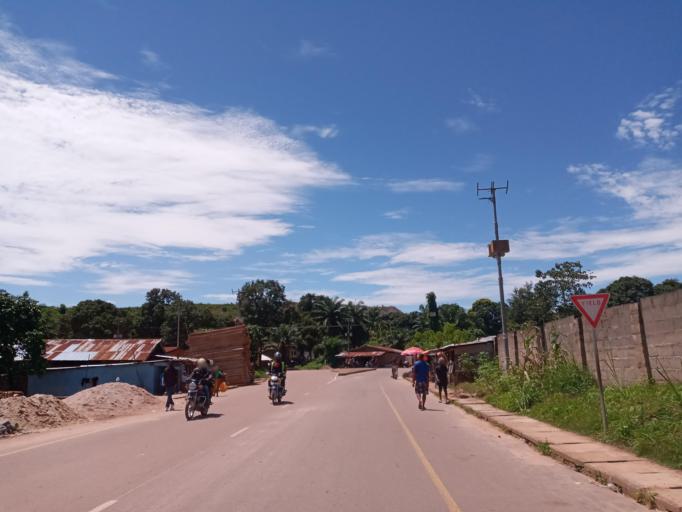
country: SL
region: Eastern Province
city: Koidu
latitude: 8.6392
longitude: -10.9699
